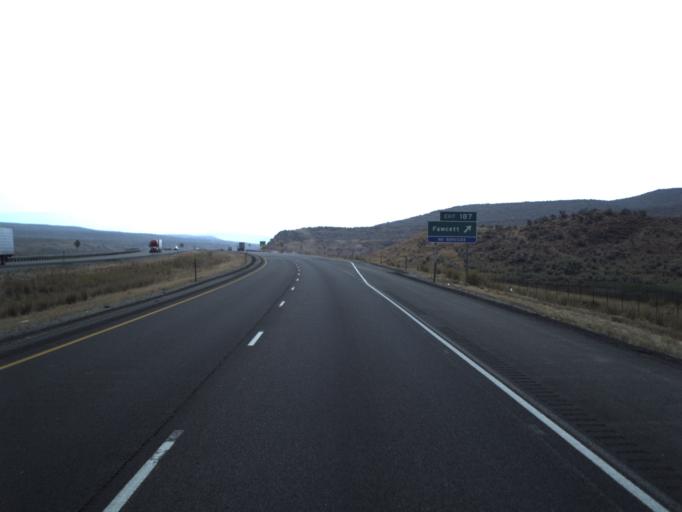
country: US
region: Wyoming
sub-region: Uinta County
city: Evanston
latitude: 41.1577
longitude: -111.1428
